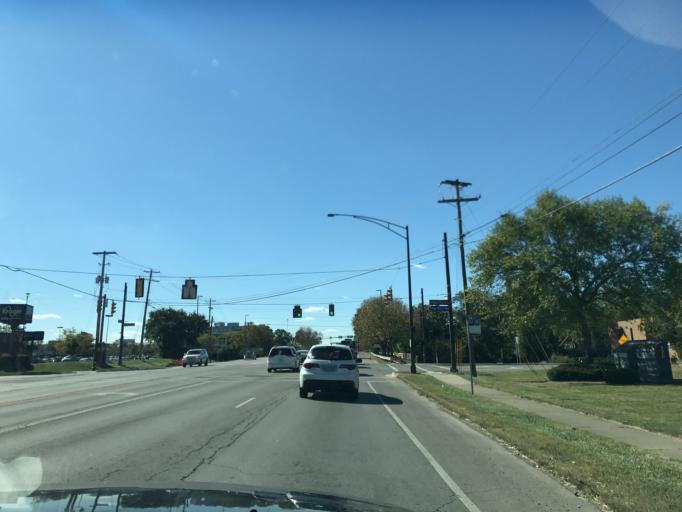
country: US
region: Ohio
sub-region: Franklin County
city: Dublin
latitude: 40.0993
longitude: -83.1204
